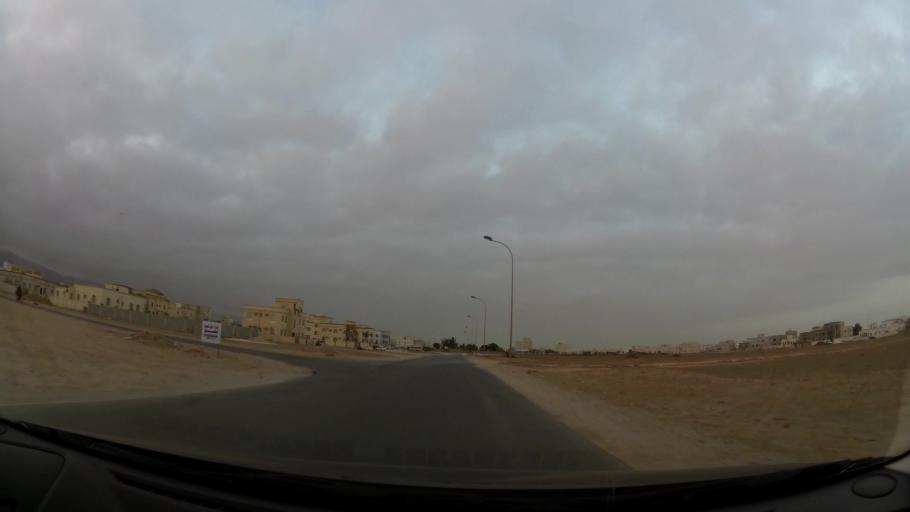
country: OM
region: Zufar
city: Salalah
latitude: 17.0389
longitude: 54.0299
